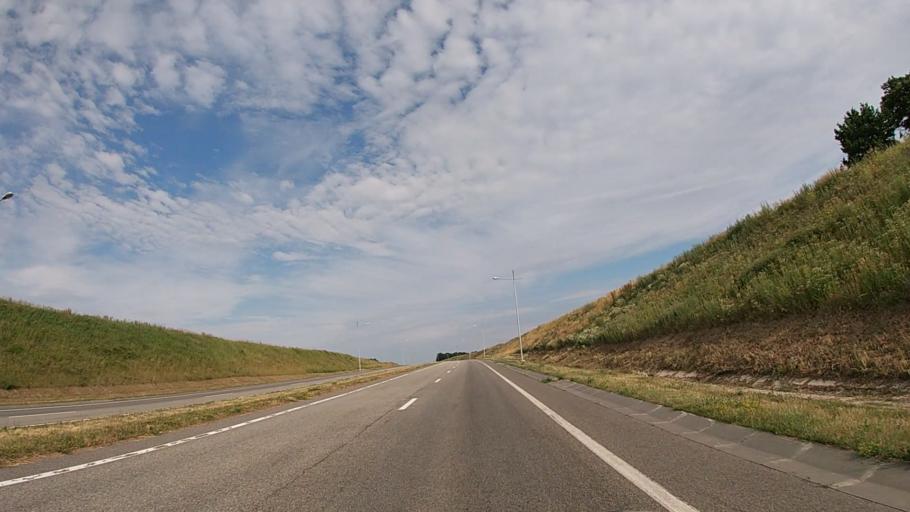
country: RU
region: Belgorod
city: Tomarovka
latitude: 50.7048
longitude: 36.2199
